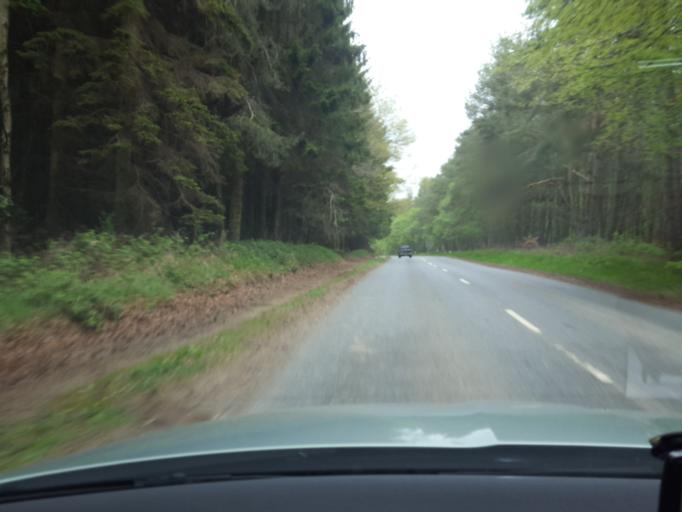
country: GB
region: Scotland
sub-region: Angus
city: Brechin
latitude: 56.7904
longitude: -2.6476
